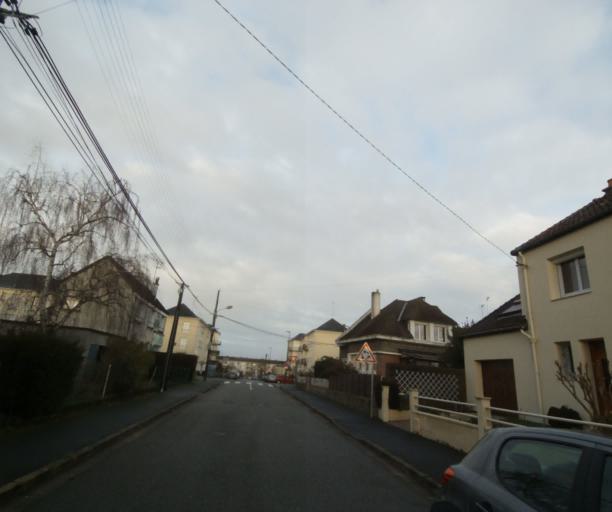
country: FR
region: Pays de la Loire
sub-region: Departement de la Sarthe
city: Le Mans
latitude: 47.9783
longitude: 0.2225
